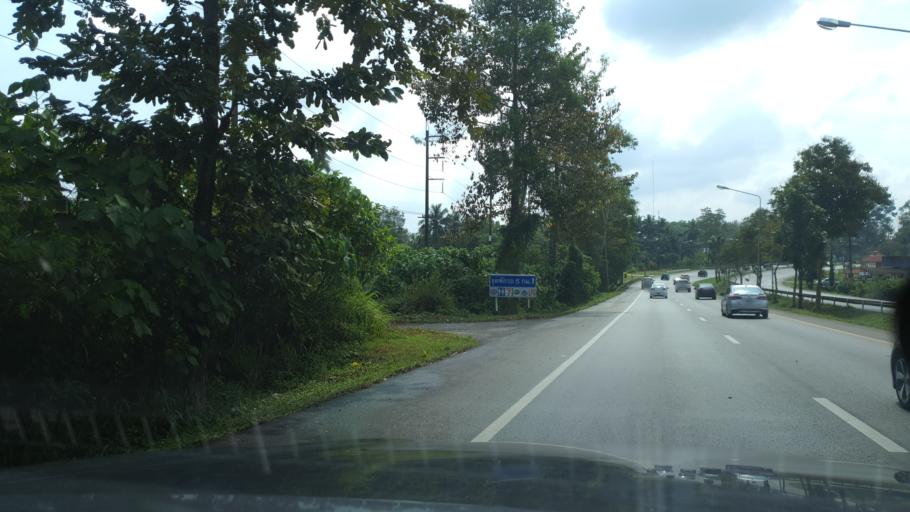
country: TH
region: Chumphon
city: Chumphon
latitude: 10.5409
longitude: 99.1167
